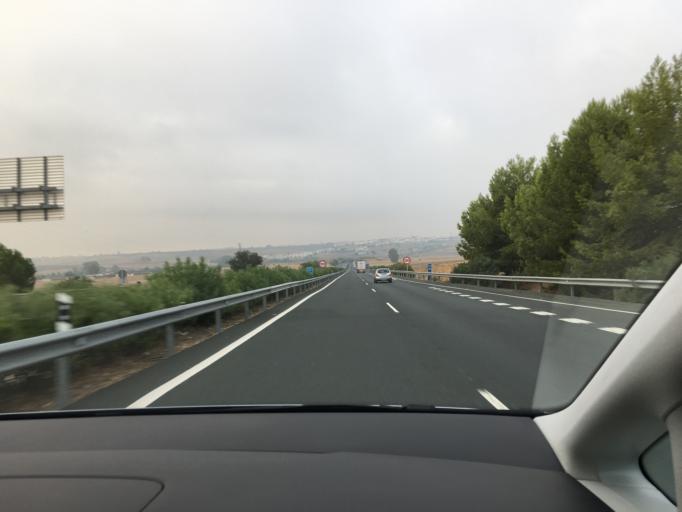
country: ES
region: Andalusia
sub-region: Province of Cordoba
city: La Carlota
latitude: 37.6944
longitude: -4.9201
